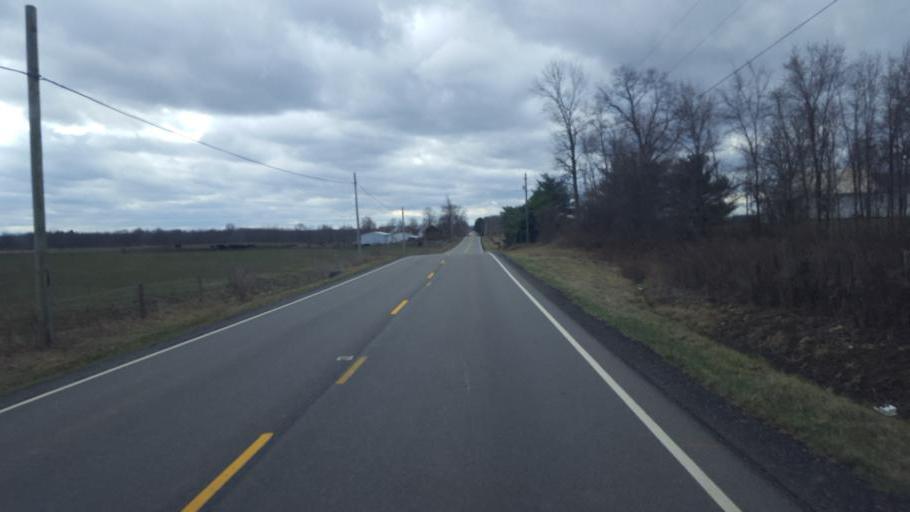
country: US
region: Ohio
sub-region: Licking County
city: Utica
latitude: 40.2876
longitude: -82.5138
